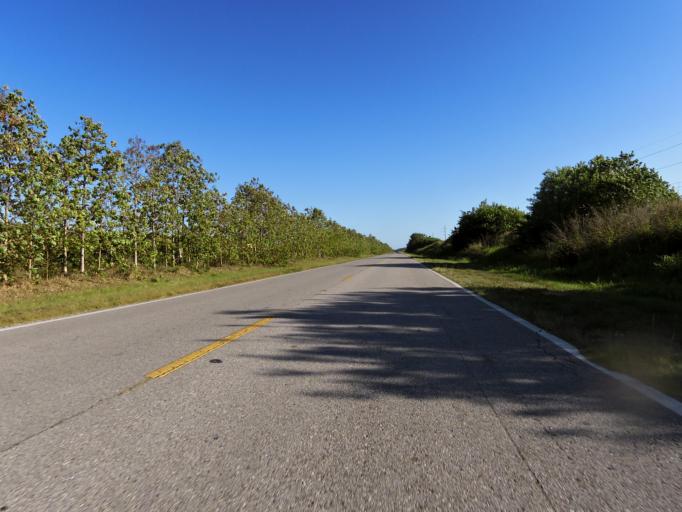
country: US
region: Florida
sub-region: Collier County
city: Immokalee
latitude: 26.3300
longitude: -81.4166
